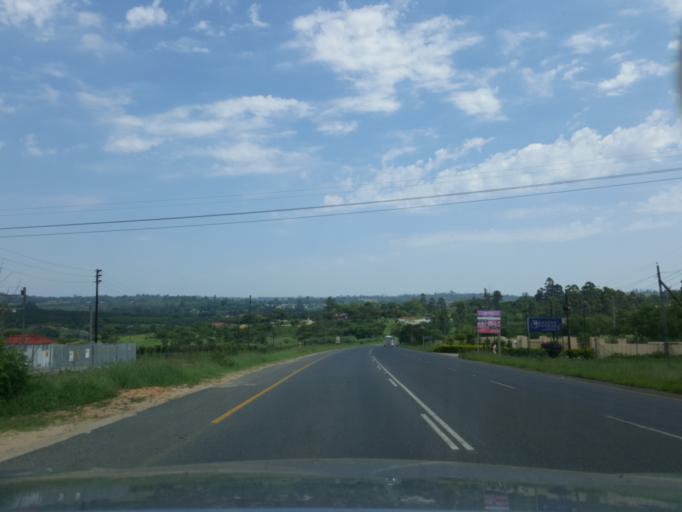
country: ZA
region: Mpumalanga
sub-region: Ehlanzeni District
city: White River
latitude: -25.3595
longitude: 31.0717
